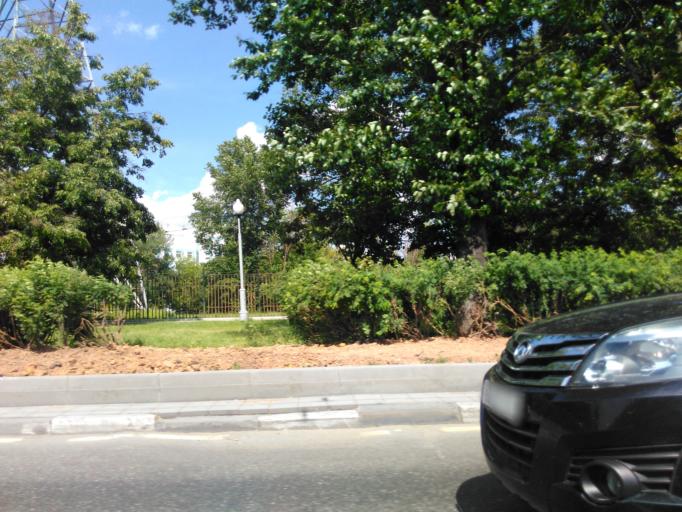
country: RU
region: Moscow
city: Nagornyy
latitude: 55.6604
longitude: 37.6374
